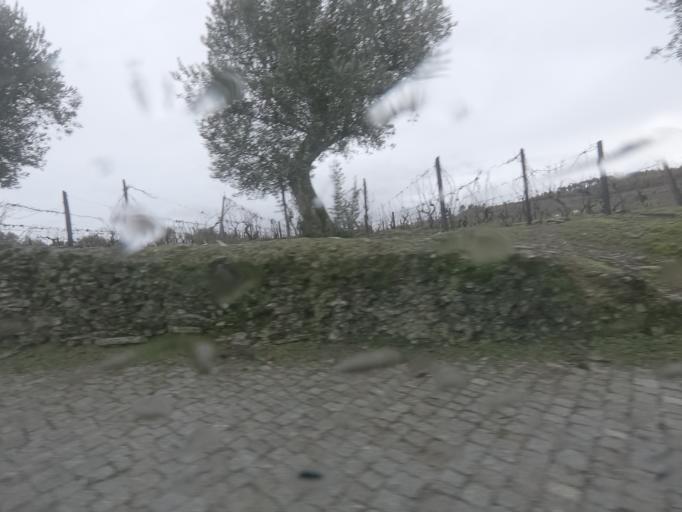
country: PT
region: Vila Real
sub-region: Peso da Regua
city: Peso da Regua
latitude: 41.1802
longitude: -7.7187
